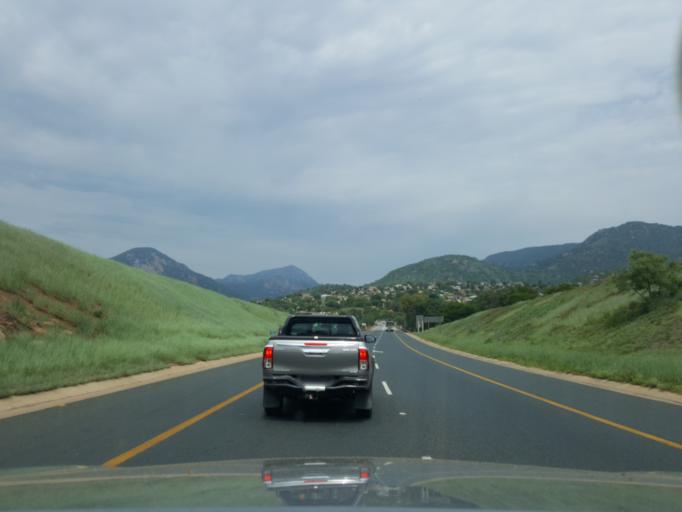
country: SZ
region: Hhohho
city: Ntfonjeni
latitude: -25.5376
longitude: 31.3160
